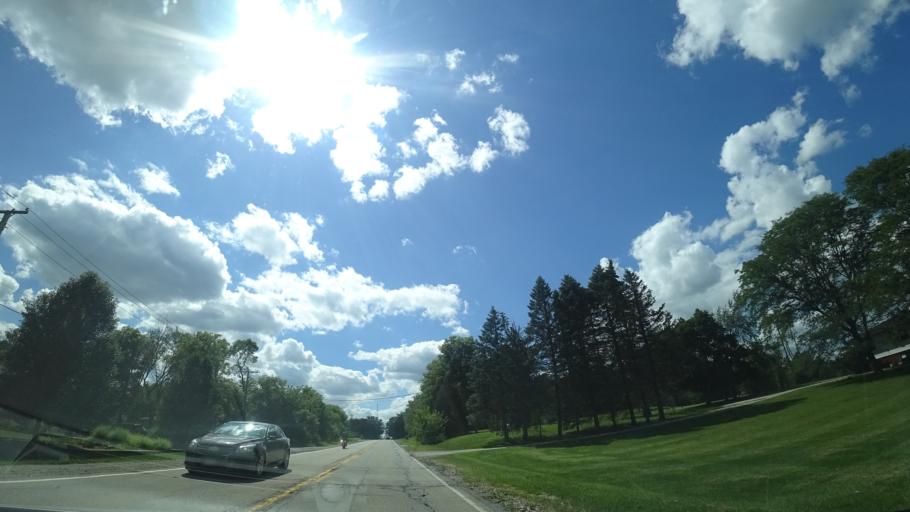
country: US
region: Illinois
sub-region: Will County
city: New Lenox
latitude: 41.5488
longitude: -87.9333
